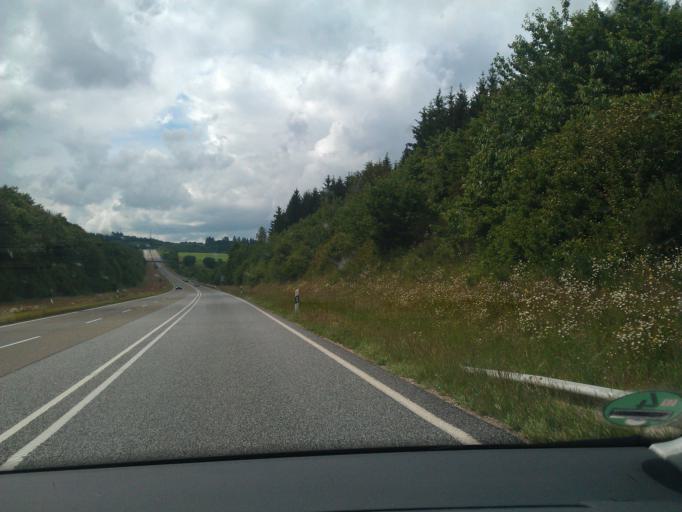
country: DE
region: Rheinland-Pfalz
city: Winterspelt
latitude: 50.2209
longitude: 6.2235
